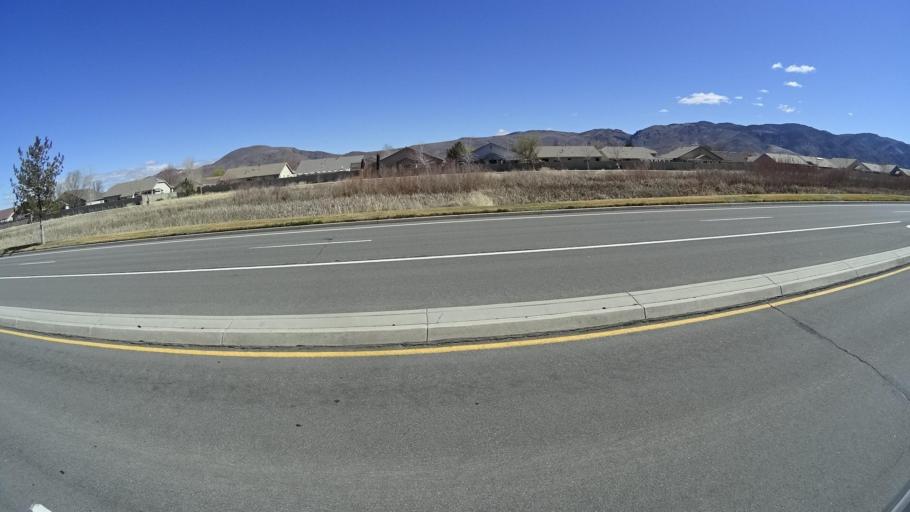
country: US
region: Nevada
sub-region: Washoe County
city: Sparks
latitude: 39.4289
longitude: -119.7527
